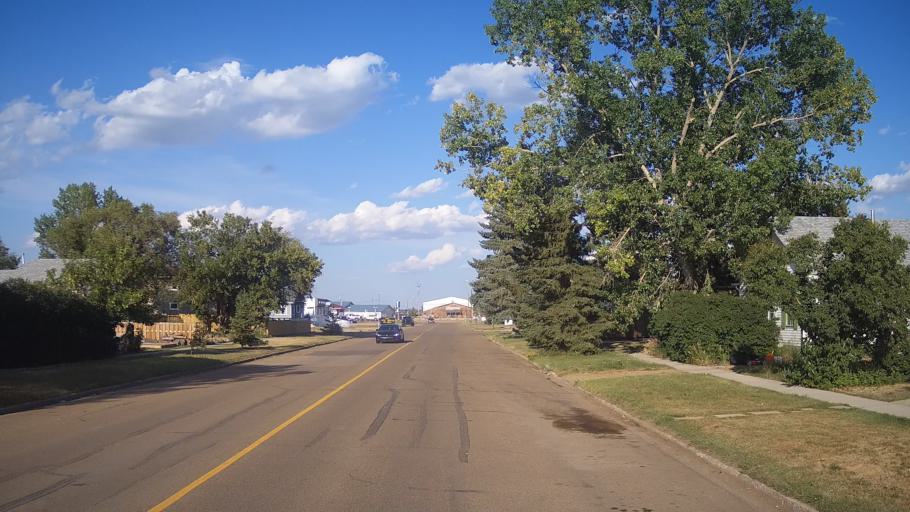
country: CA
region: Alberta
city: Hanna
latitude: 51.6442
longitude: -111.9221
